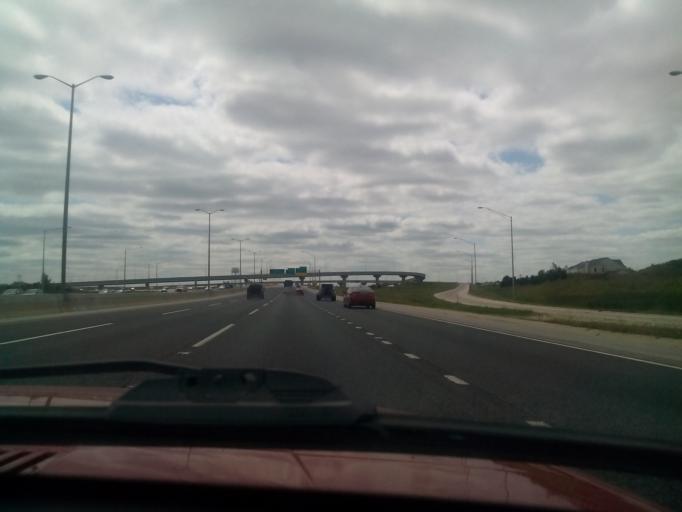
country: US
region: Illinois
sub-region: Will County
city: Bolingbrook
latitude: 41.7124
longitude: -88.0325
